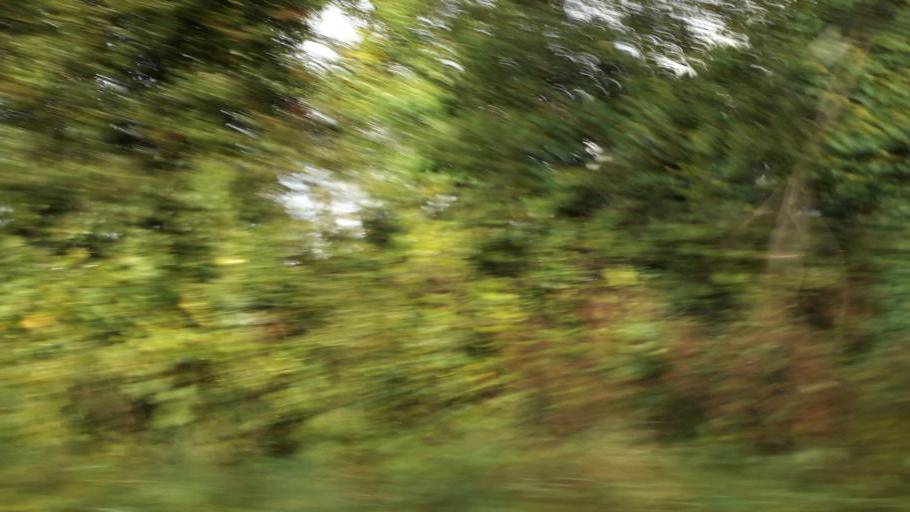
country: IE
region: Connaught
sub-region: Roscommon
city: Roscommon
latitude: 53.7739
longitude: -8.1265
